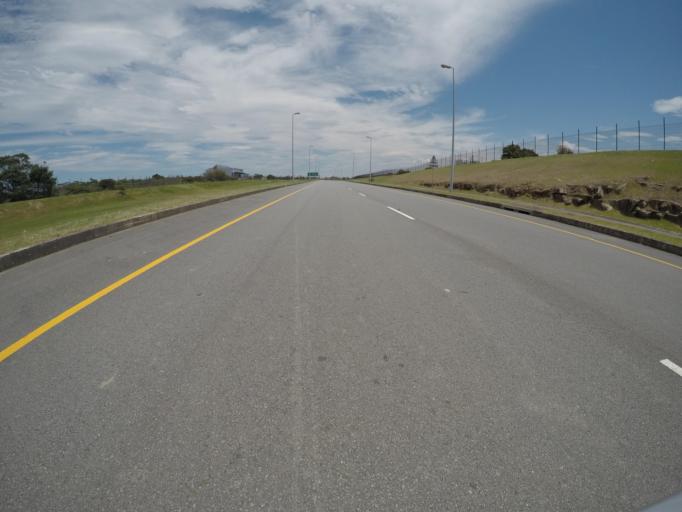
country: ZA
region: Eastern Cape
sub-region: Buffalo City Metropolitan Municipality
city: East London
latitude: -33.0560
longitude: 27.8378
